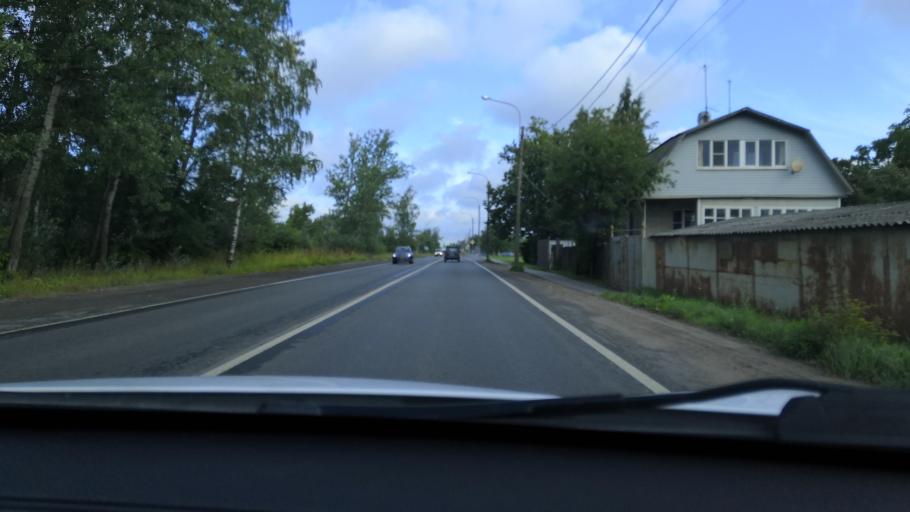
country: RU
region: St.-Petersburg
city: Tyarlevo
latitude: 59.7063
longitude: 30.4384
